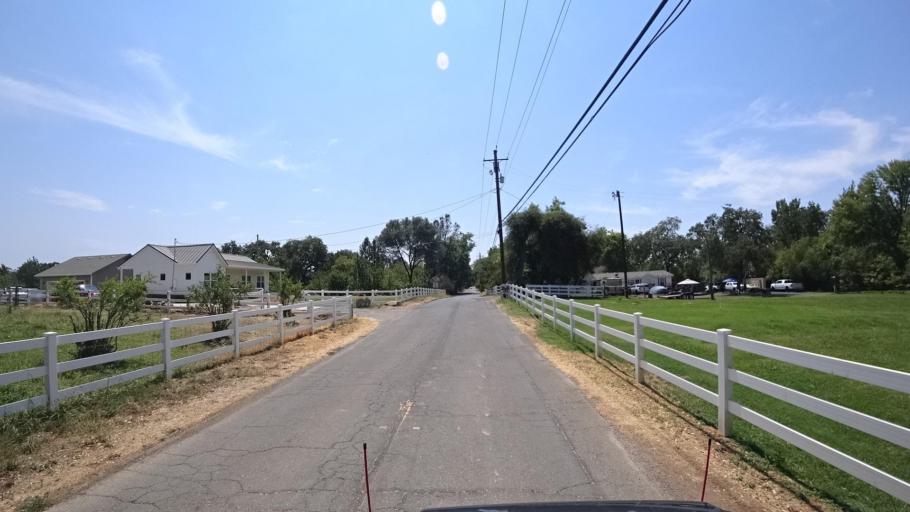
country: US
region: California
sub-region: Placer County
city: Loomis
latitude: 38.8220
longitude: -121.2195
